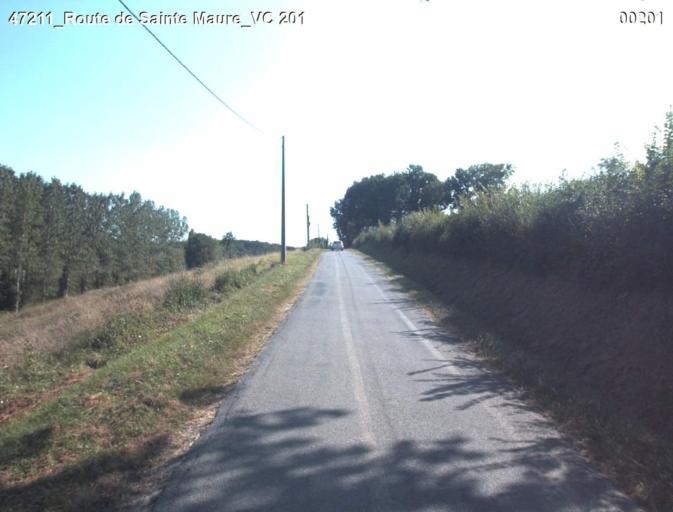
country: FR
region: Aquitaine
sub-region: Departement du Lot-et-Garonne
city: Mezin
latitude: 44.0377
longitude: 0.1956
